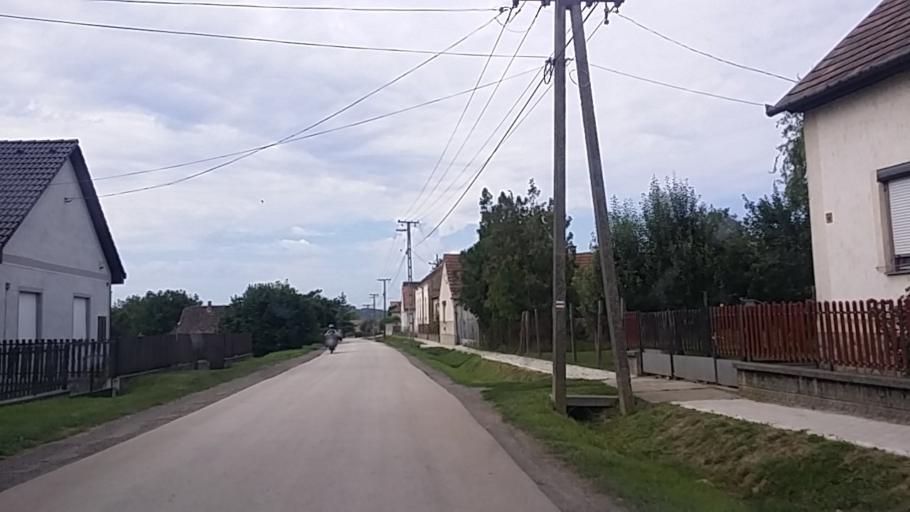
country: HU
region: Somogy
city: Taszar
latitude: 46.3511
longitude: 17.9929
